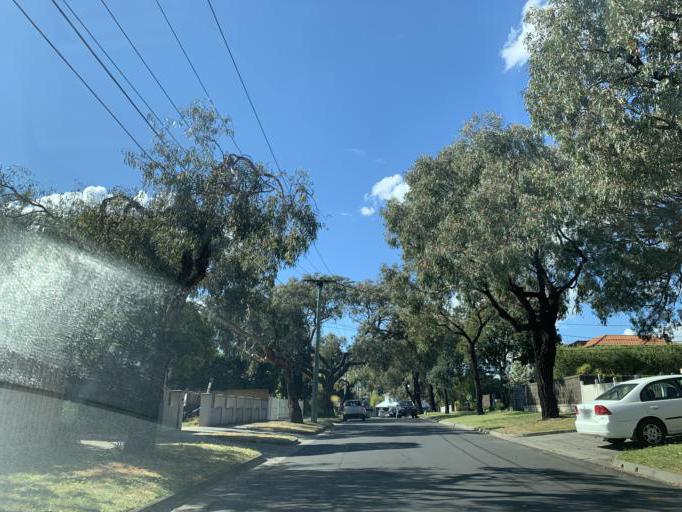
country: AU
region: Victoria
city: Hampton
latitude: -37.9517
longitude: 145.0178
